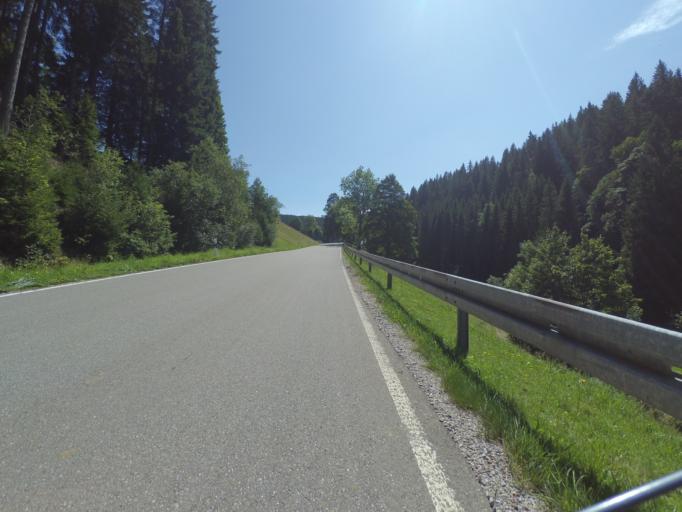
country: DE
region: Baden-Wuerttemberg
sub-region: Freiburg Region
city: Furtwangen im Schwarzwald
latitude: 48.0273
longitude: 8.2000
